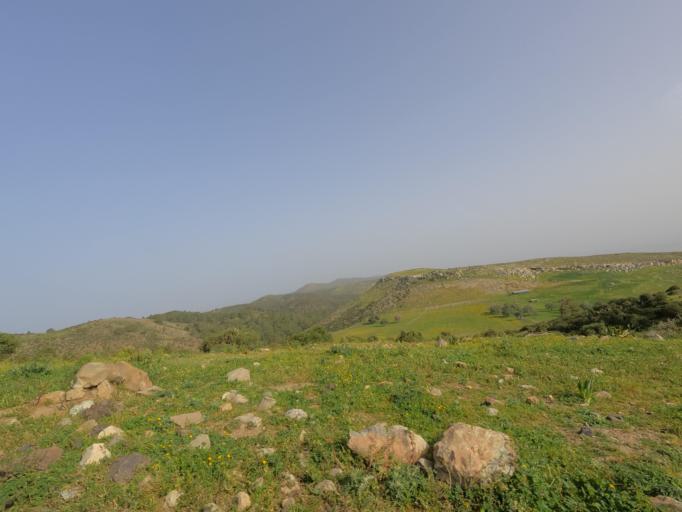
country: CY
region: Pafos
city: Polis
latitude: 34.9945
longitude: 32.3502
